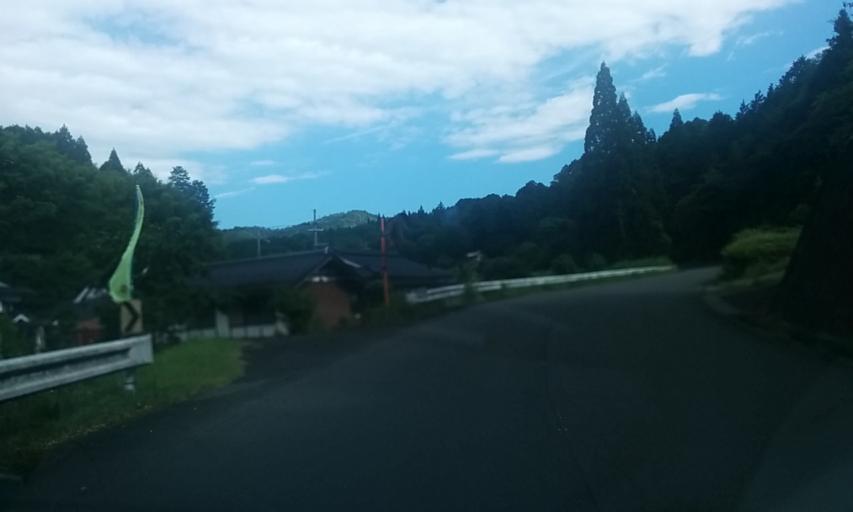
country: JP
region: Kyoto
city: Fukuchiyama
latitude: 35.3575
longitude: 135.1432
